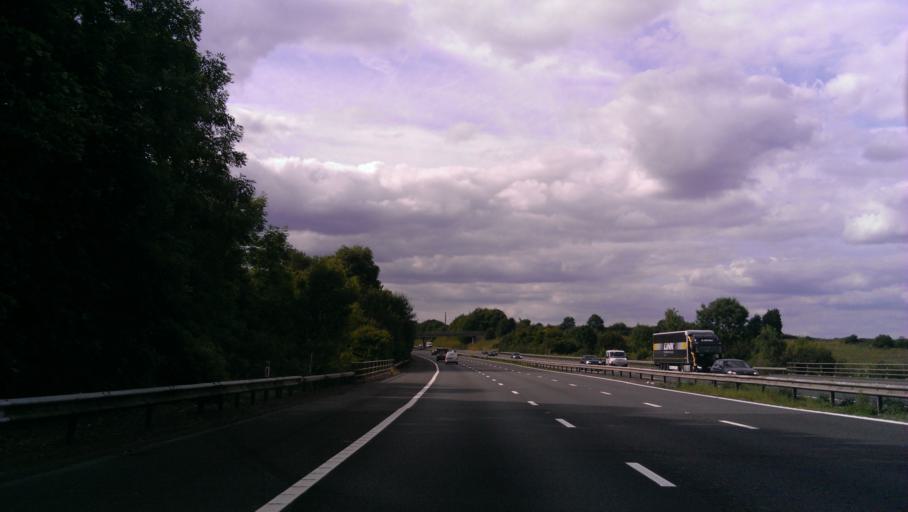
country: GB
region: England
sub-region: Kent
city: Longfield
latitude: 51.3604
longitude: 0.2685
